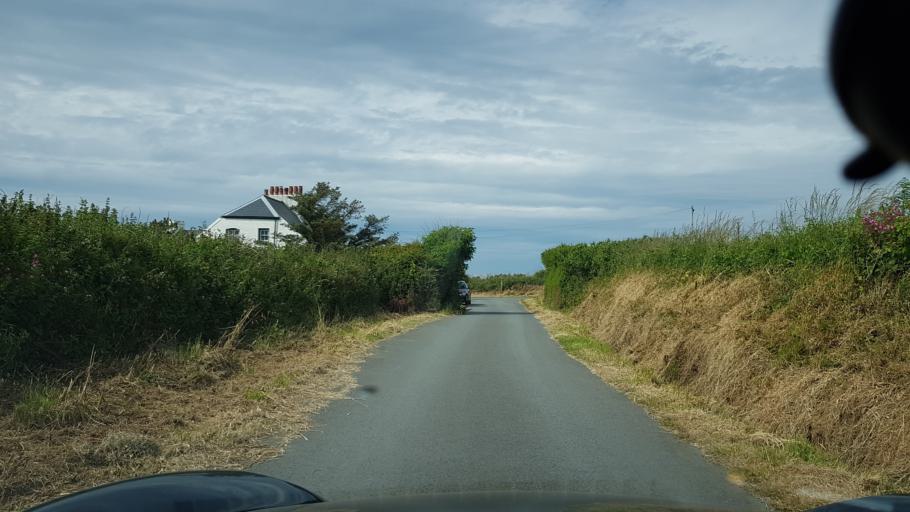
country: GB
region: Wales
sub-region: Pembrokeshire
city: Dale
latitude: 51.7312
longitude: -5.2194
